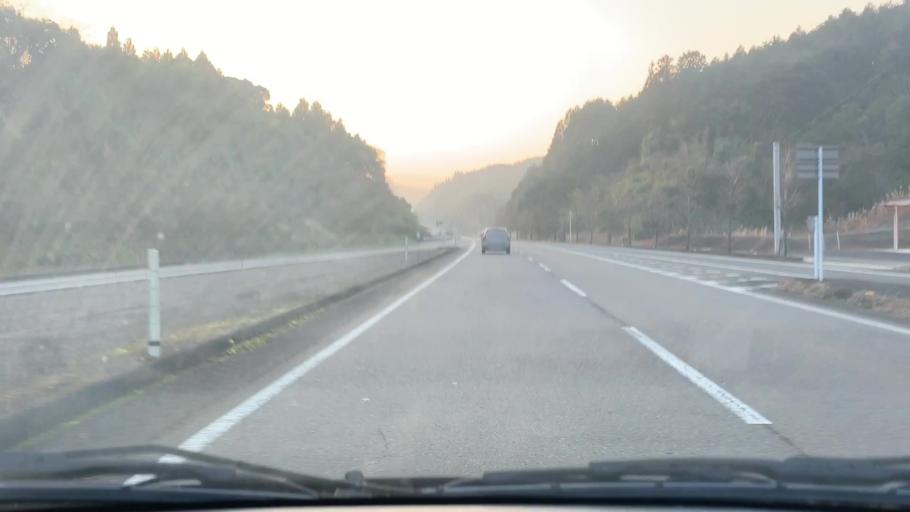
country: JP
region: Saga Prefecture
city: Imaricho-ko
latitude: 33.2633
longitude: 129.9422
